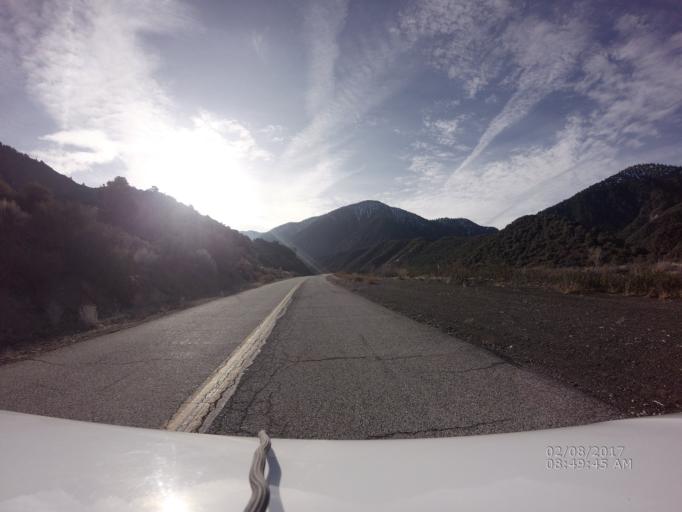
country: US
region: California
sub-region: San Bernardino County
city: Pinon Hills
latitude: 34.4077
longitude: -117.8216
